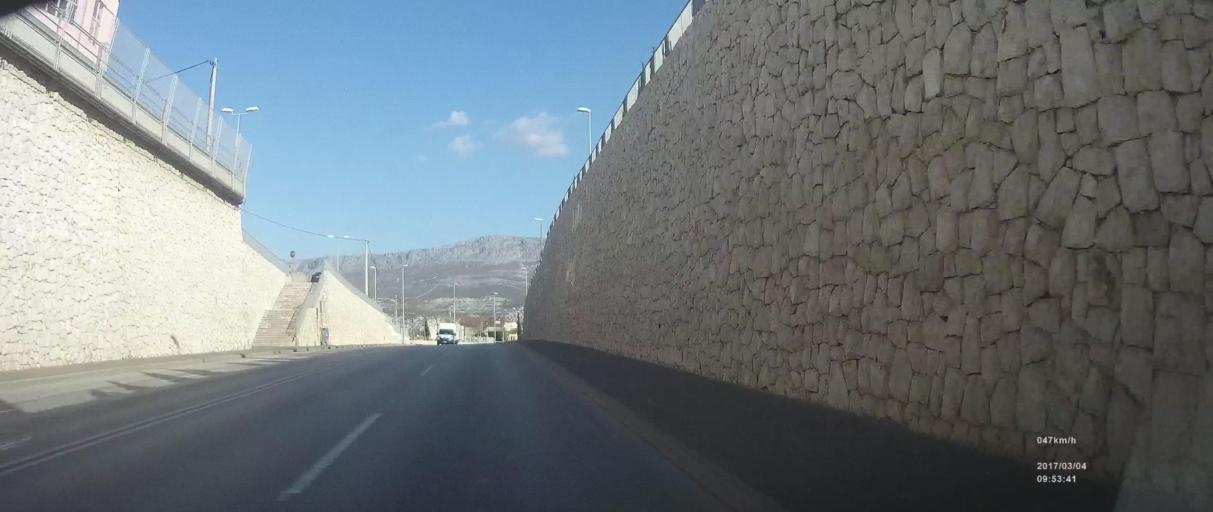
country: HR
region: Splitsko-Dalmatinska
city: Kamen
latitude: 43.5117
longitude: 16.4903
